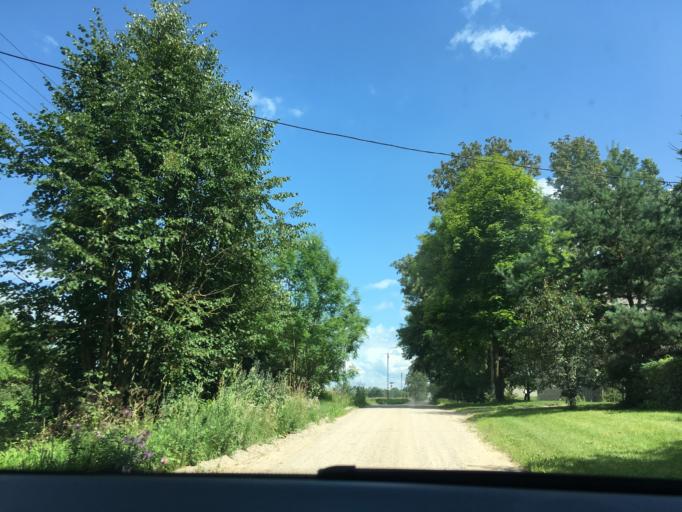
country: PL
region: Podlasie
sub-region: Powiat sejnenski
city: Krasnopol
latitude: 54.0882
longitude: 23.2460
